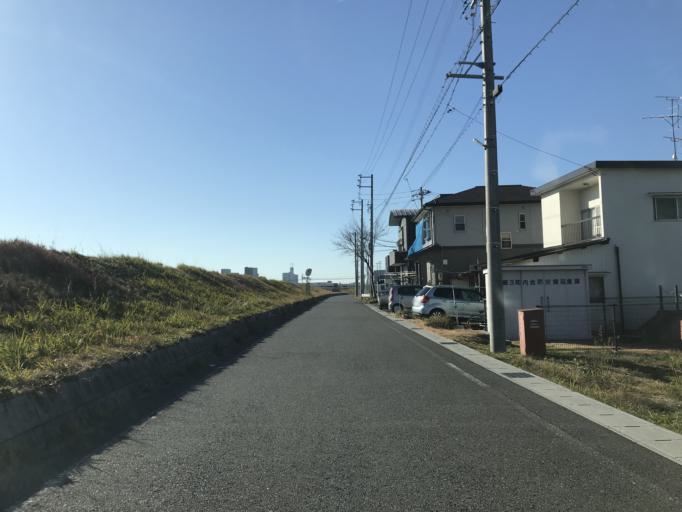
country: JP
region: Aichi
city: Nagoya-shi
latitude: 35.1971
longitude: 136.8702
